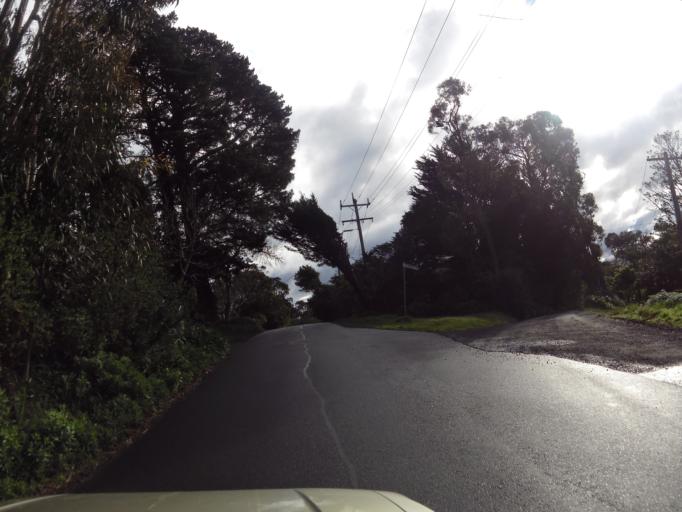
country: AU
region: Victoria
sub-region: Yarra Ranges
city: Tremont
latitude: -37.9043
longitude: 145.3237
